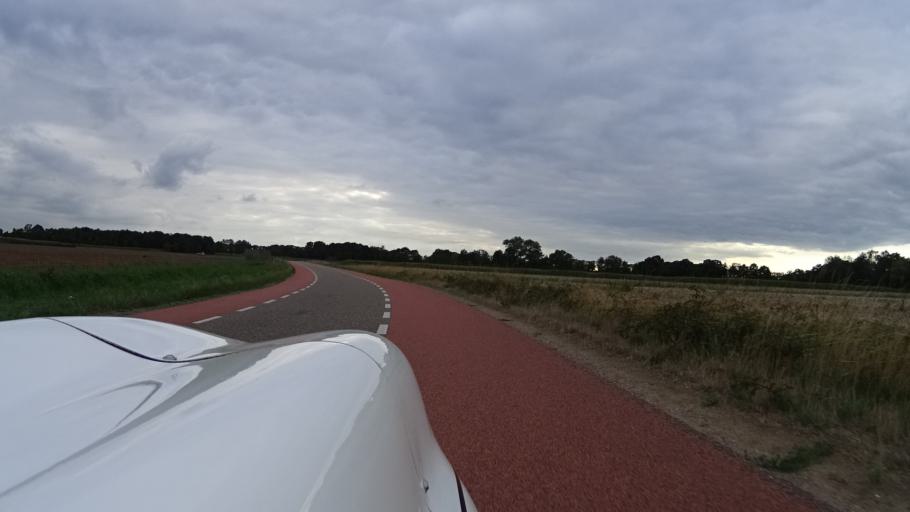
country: NL
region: North Brabant
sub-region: Gemeente Bernheze
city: Loosbroek
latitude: 51.6910
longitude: 5.4770
